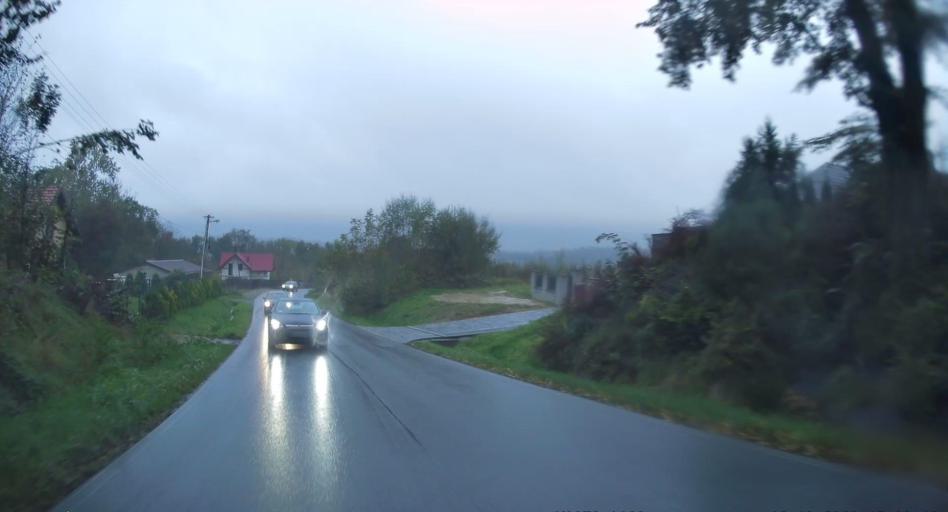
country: PL
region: Lesser Poland Voivodeship
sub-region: Powiat krakowski
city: Ochojno
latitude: 49.9601
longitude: 19.9996
